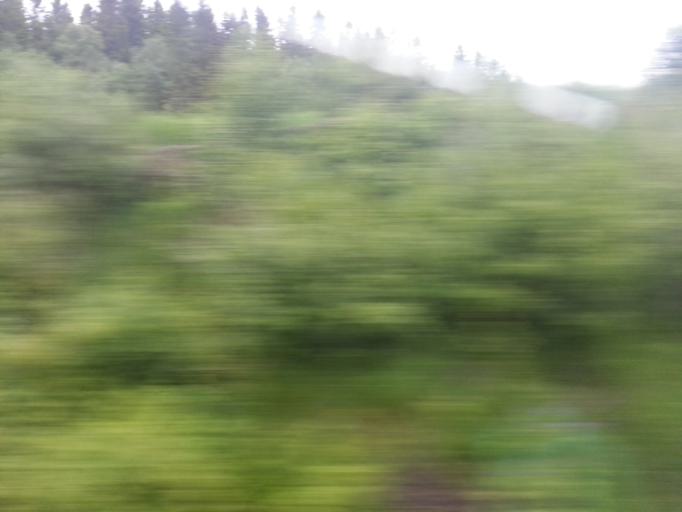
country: NO
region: Sor-Trondelag
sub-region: Melhus
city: Melhus
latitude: 63.3302
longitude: 10.3399
